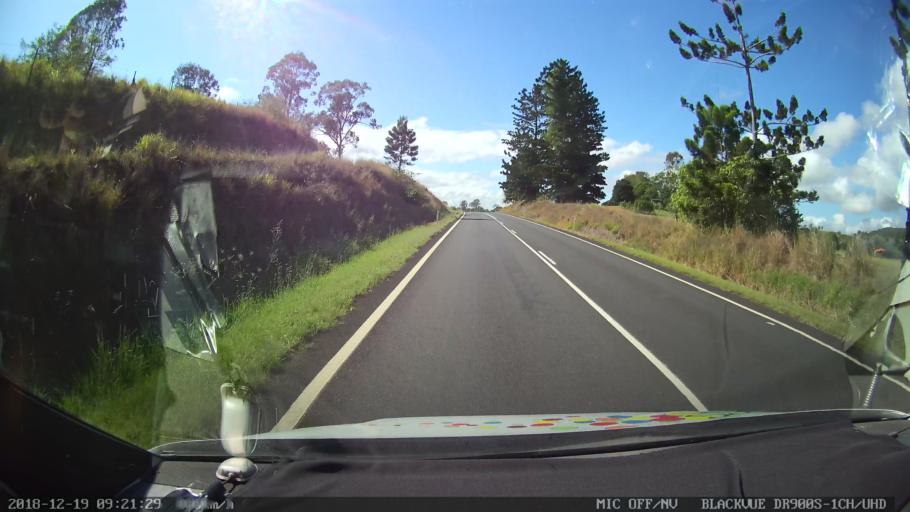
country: AU
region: New South Wales
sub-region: Kyogle
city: Kyogle
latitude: -28.5843
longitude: 152.9824
